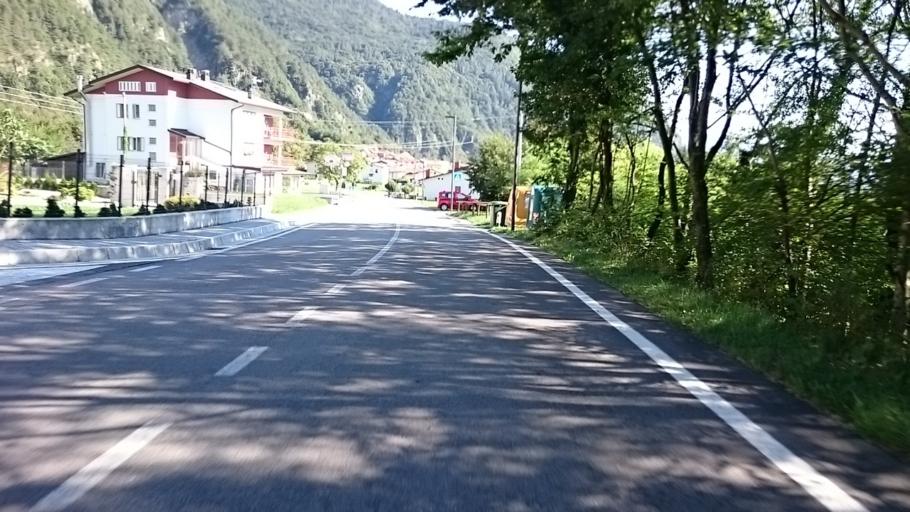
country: IT
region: Veneto
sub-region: Provincia di Belluno
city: Soverzene
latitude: 46.2097
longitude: 12.3014
